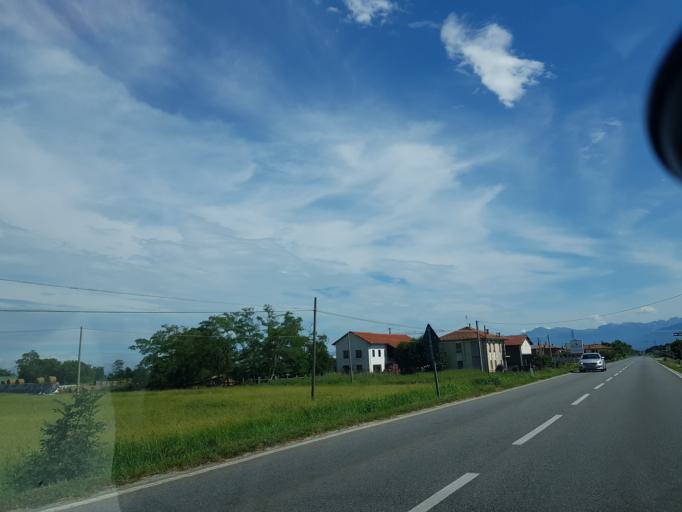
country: IT
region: Piedmont
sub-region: Provincia di Cuneo
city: Busca
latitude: 44.4941
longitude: 7.4958
